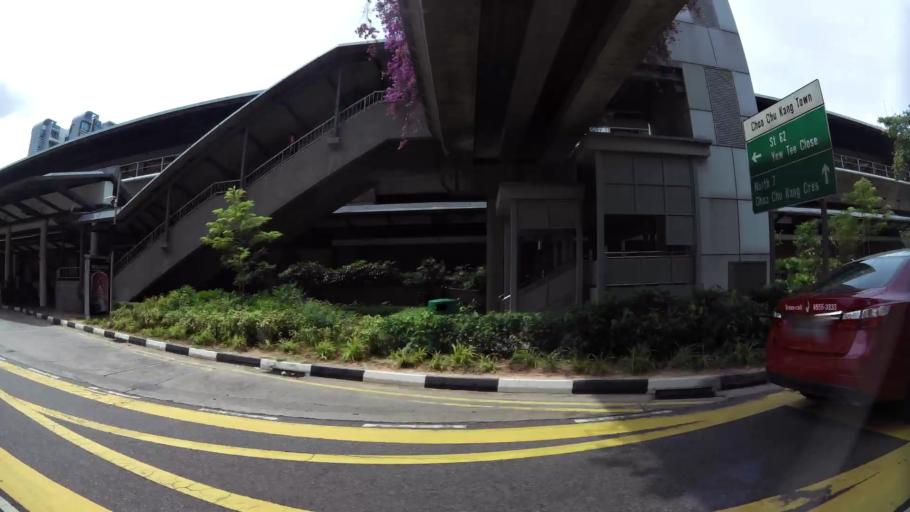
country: MY
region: Johor
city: Johor Bahru
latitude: 1.3976
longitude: 103.7478
